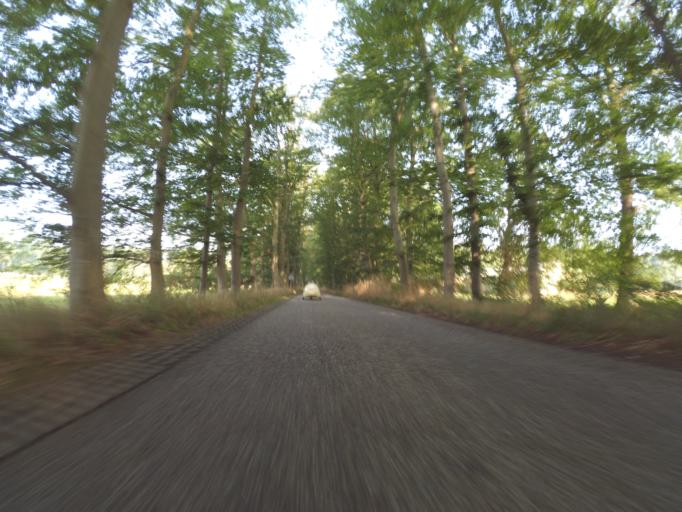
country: NL
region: Overijssel
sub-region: Gemeente Wierden
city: Wierden
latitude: 52.3289
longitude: 6.5412
